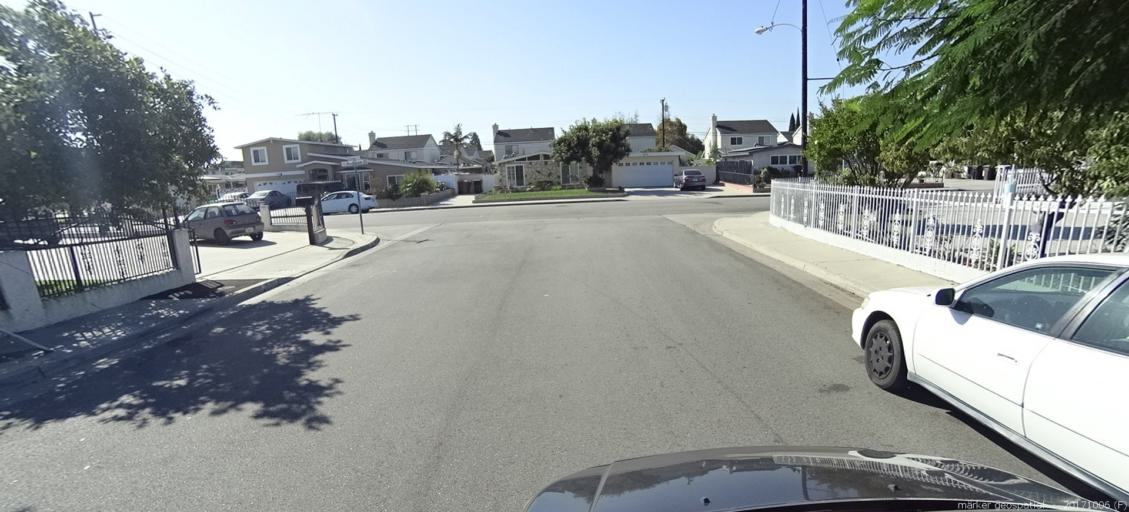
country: US
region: California
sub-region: Orange County
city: Stanton
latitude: 33.7827
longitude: -117.9802
